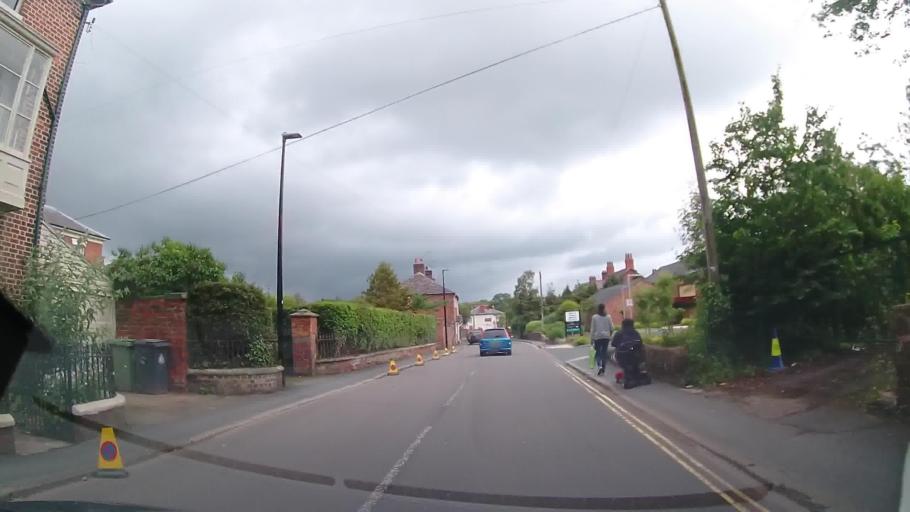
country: GB
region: England
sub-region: Shropshire
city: Wem
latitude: 52.8568
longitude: -2.7229
